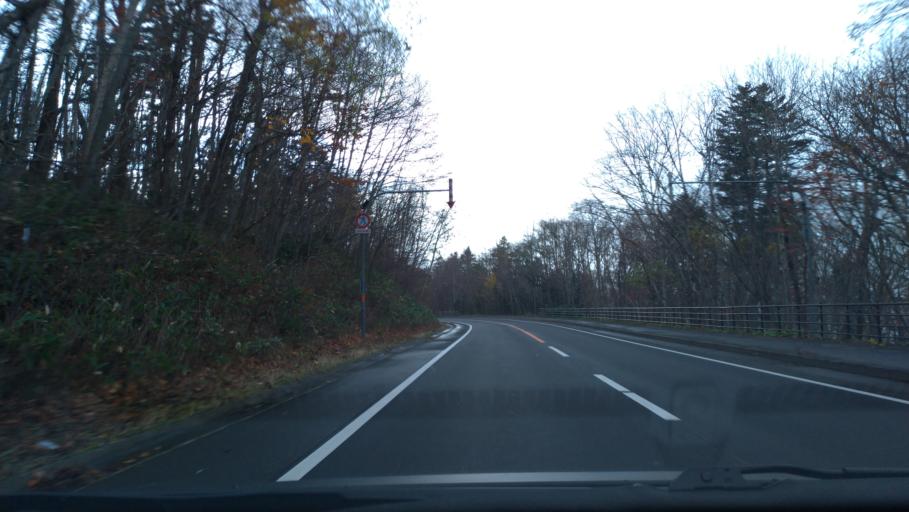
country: JP
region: Hokkaido
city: Shiraoi
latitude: 42.7347
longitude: 141.3471
